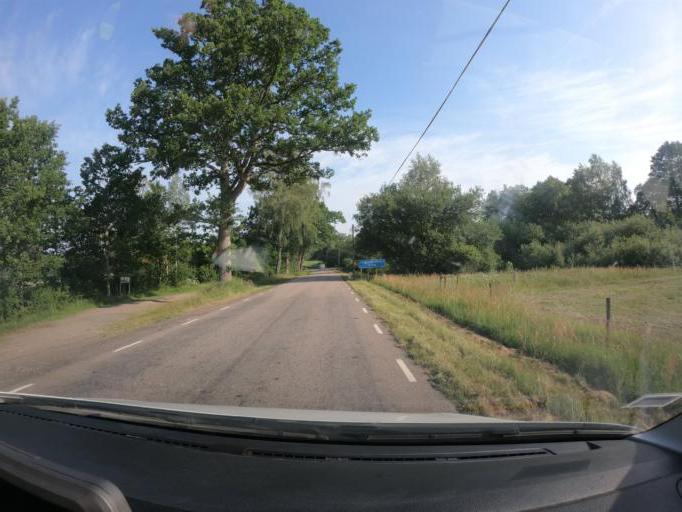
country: SE
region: Skane
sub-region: Orkelljunga Kommun
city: OErkelljunga
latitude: 56.2865
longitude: 13.3907
